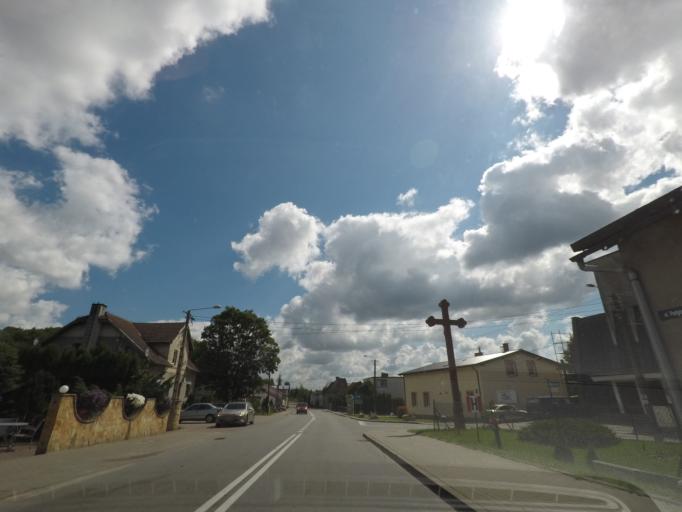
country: PL
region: Pomeranian Voivodeship
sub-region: Powiat wejherowski
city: Leczyce
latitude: 54.5942
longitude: 17.8584
